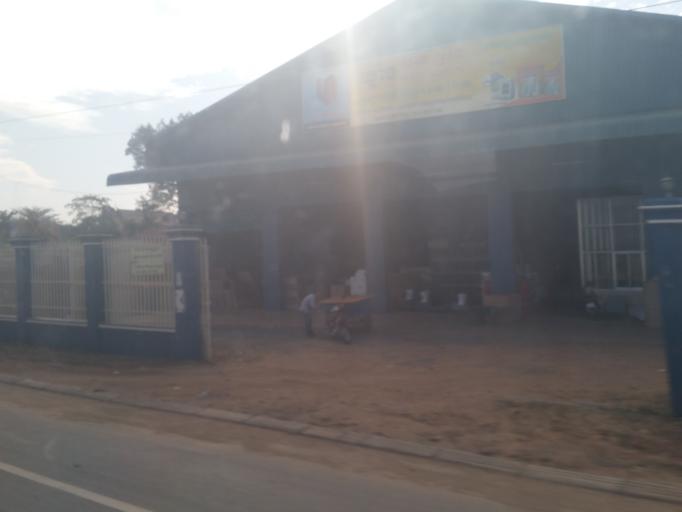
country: KH
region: Phnom Penh
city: Phnom Penh
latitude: 11.6697
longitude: 104.9145
